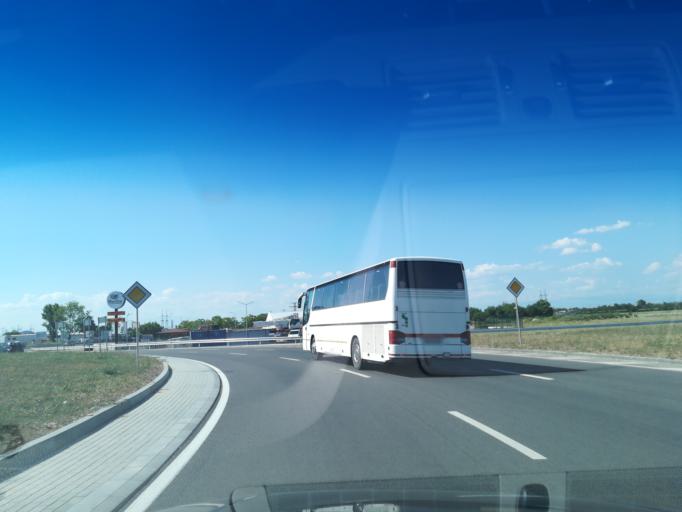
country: BG
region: Plovdiv
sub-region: Obshtina Plovdiv
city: Plovdiv
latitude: 42.0992
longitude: 24.7891
